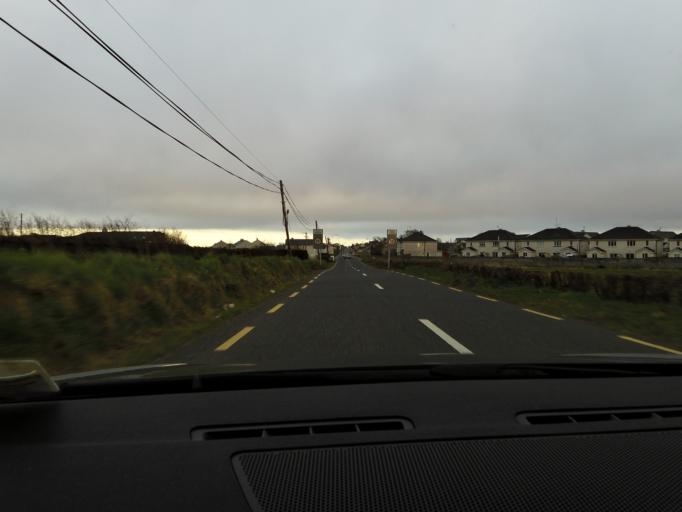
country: IE
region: Connaught
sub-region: Sligo
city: Ballymote
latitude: 53.9984
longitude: -8.5289
